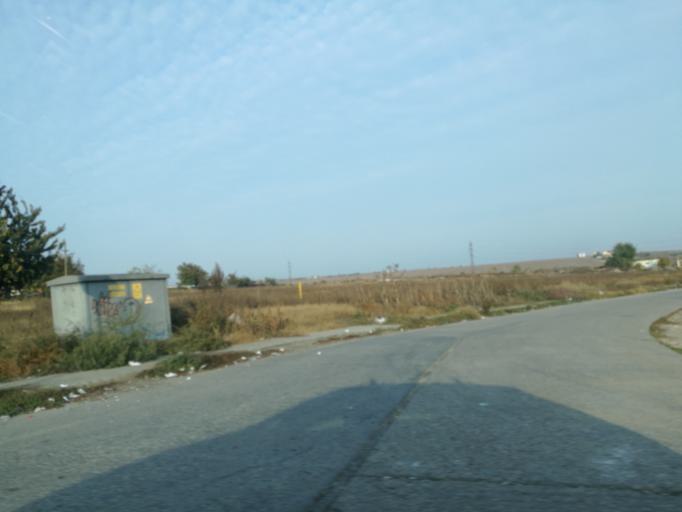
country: RO
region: Constanta
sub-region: Municipiul Constanta
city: Palazu Mare
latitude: 44.2019
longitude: 28.6089
